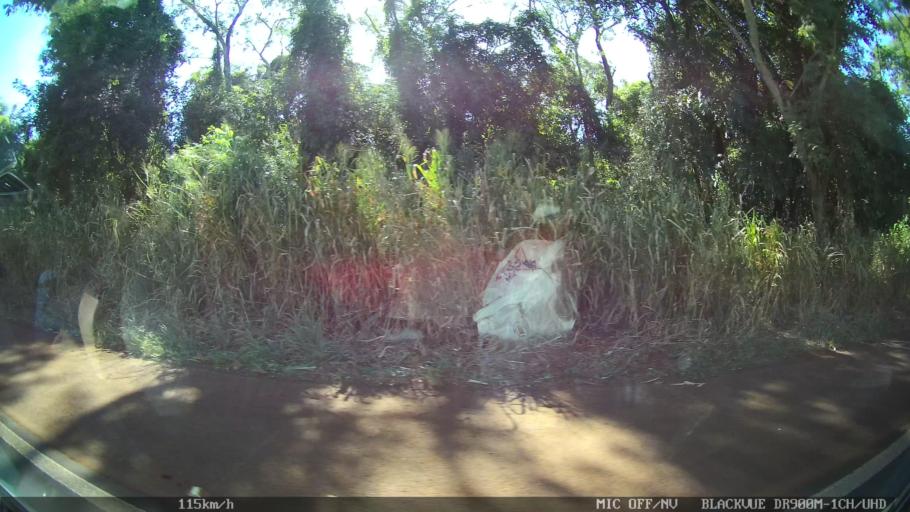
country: BR
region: Sao Paulo
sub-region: Guaira
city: Guaira
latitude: -20.4433
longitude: -48.3326
